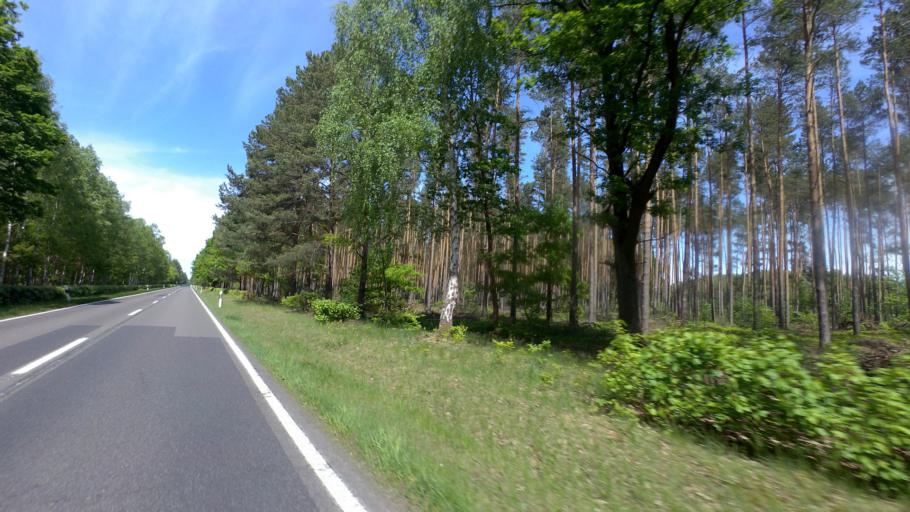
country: DE
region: Brandenburg
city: Sperenberg
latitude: 52.1091
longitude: 13.3718
